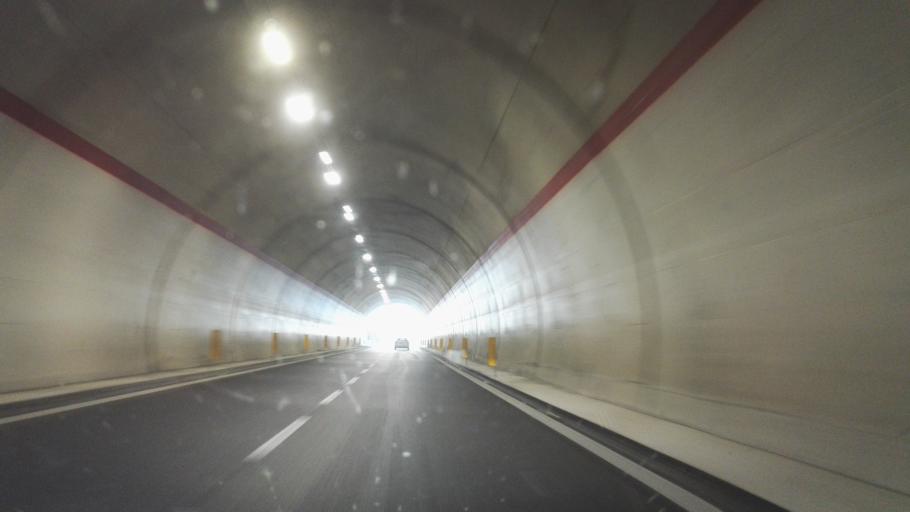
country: IT
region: Calabria
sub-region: Provincia di Reggio Calabria
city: Roccella Ionica
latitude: 38.3293
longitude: 16.4118
